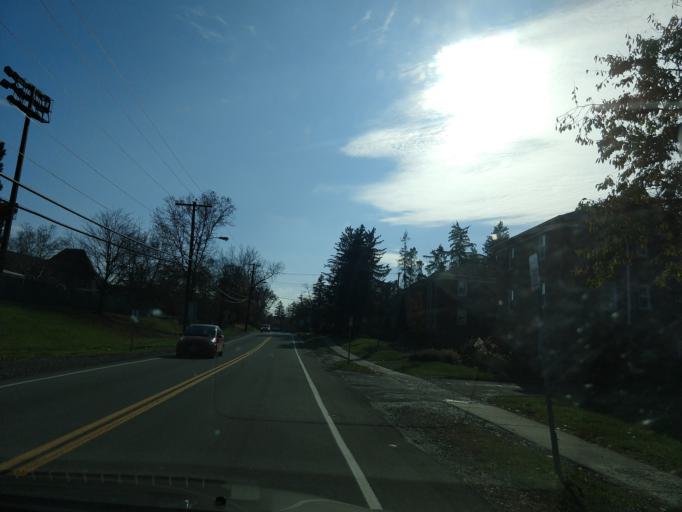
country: US
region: New York
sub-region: Tompkins County
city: Cayuga Heights
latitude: 42.4571
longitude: -76.4817
